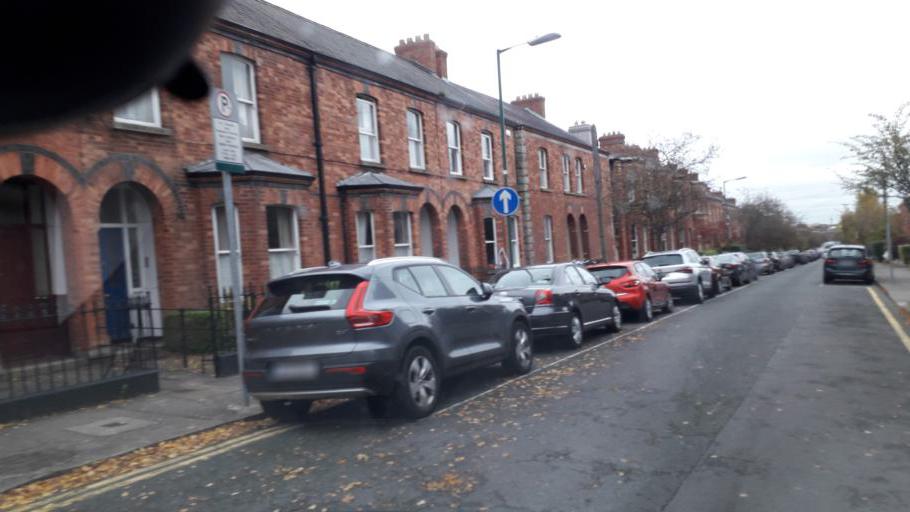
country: IE
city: Milltown
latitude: 53.3182
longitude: -6.2533
